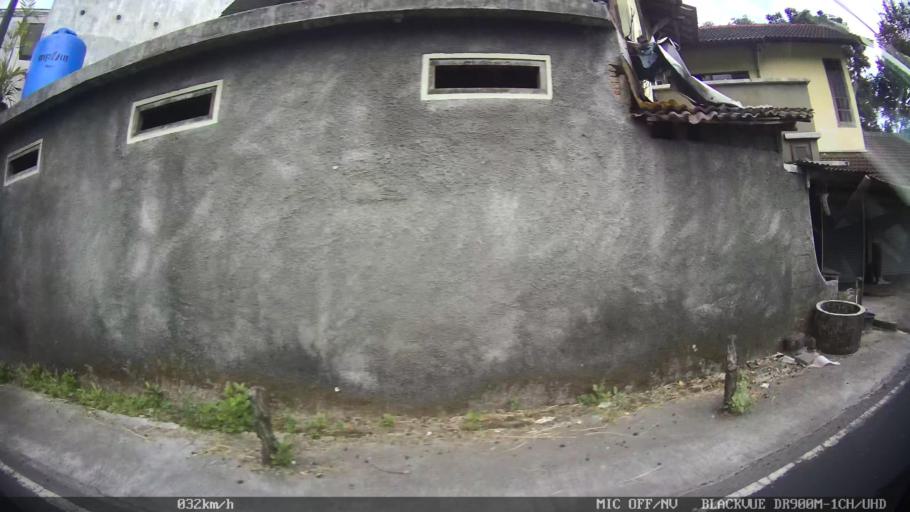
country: ID
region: Daerah Istimewa Yogyakarta
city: Depok
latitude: -7.6837
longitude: 110.4367
